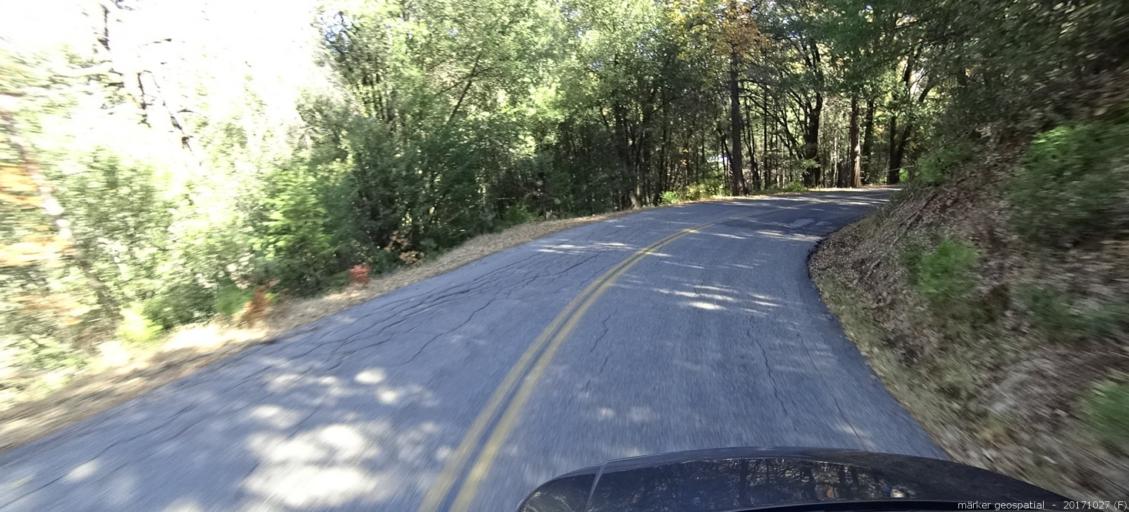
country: US
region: California
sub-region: Shasta County
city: Shingletown
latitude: 40.7480
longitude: -121.9455
